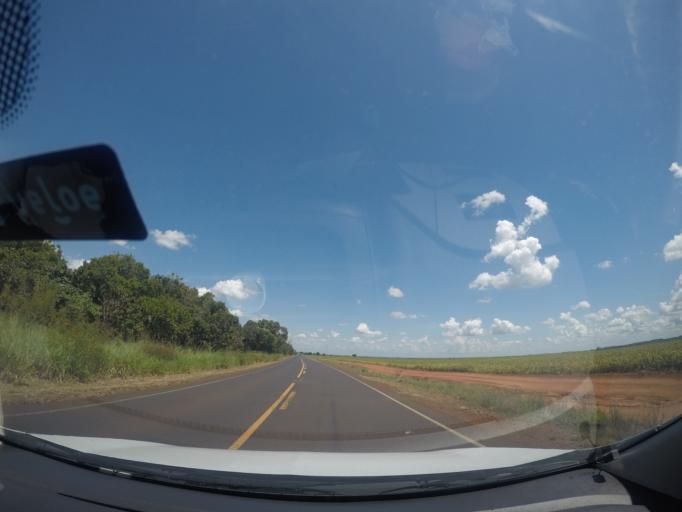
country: BR
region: Minas Gerais
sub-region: Frutal
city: Frutal
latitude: -19.7059
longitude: -48.7702
